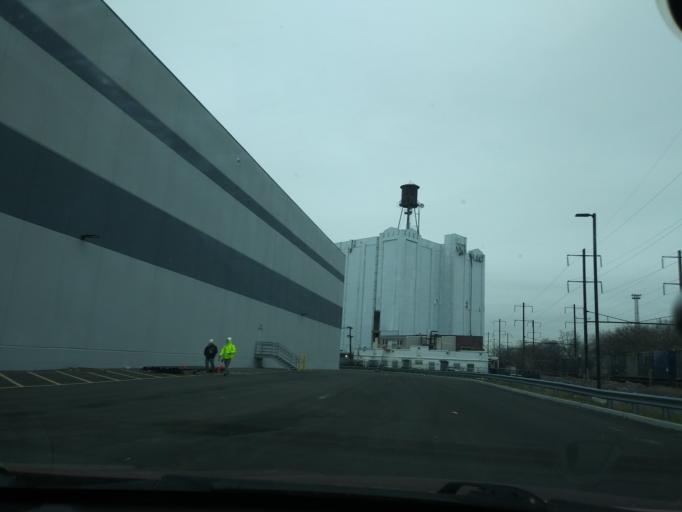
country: US
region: New Jersey
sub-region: Essex County
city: Newark
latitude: 40.7154
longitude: -74.1759
